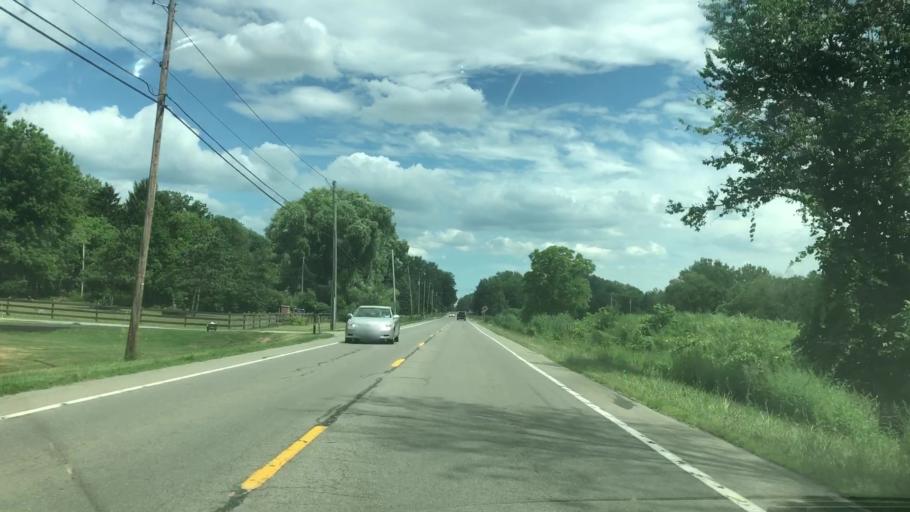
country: US
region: New York
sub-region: Monroe County
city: Webster
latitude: 43.1598
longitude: -77.4158
